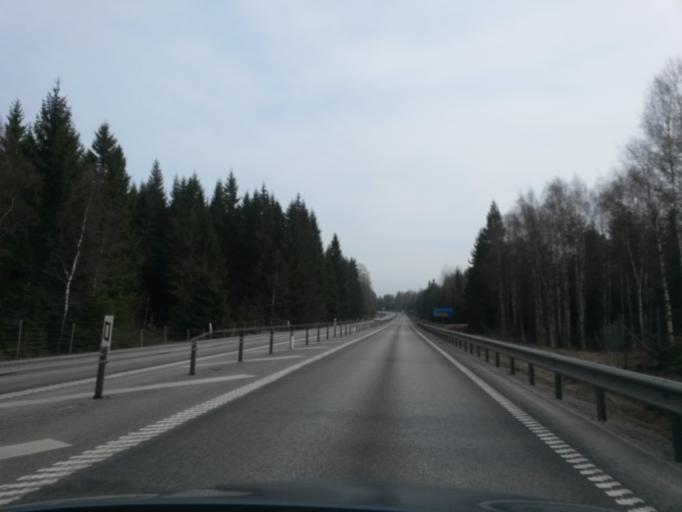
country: SE
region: OErebro
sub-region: Laxa Kommun
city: Laxa
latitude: 58.9589
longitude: 14.5221
